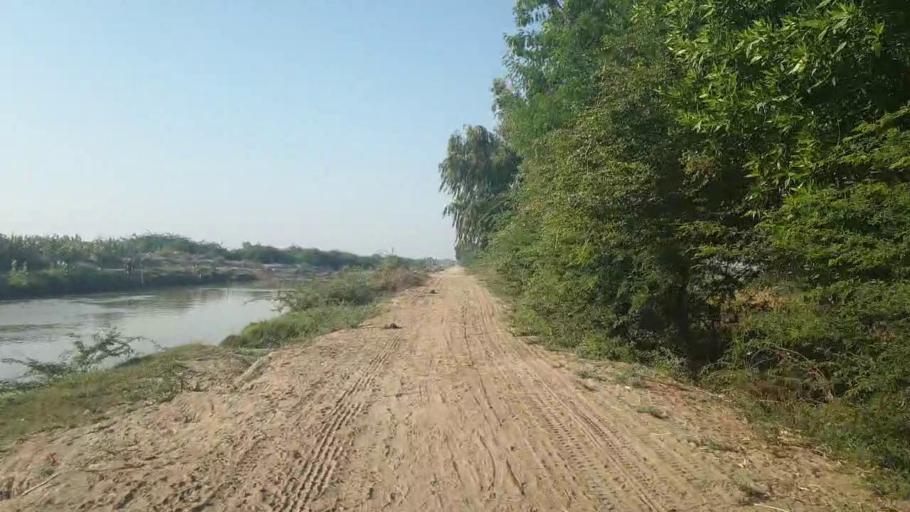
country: PK
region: Sindh
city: Tando Bago
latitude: 24.7285
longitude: 68.9266
